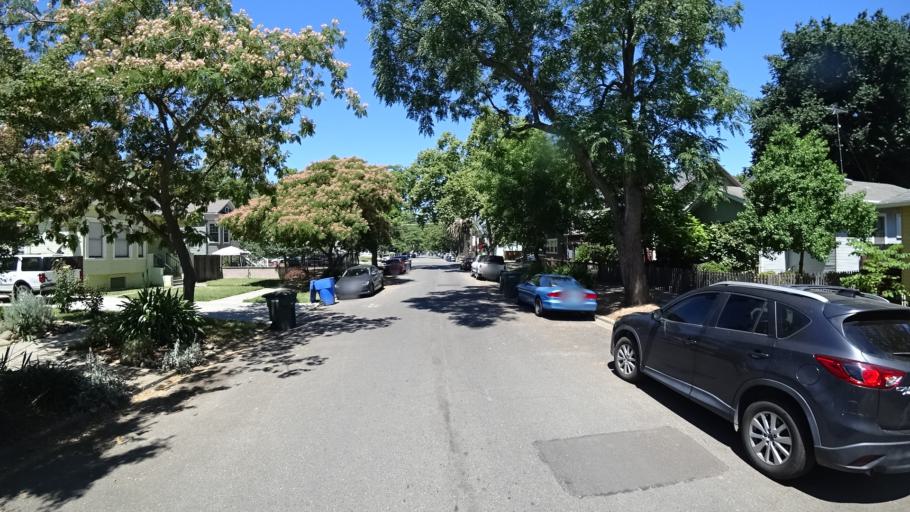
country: US
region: California
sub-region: Sacramento County
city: Sacramento
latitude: 38.5529
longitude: -121.4643
